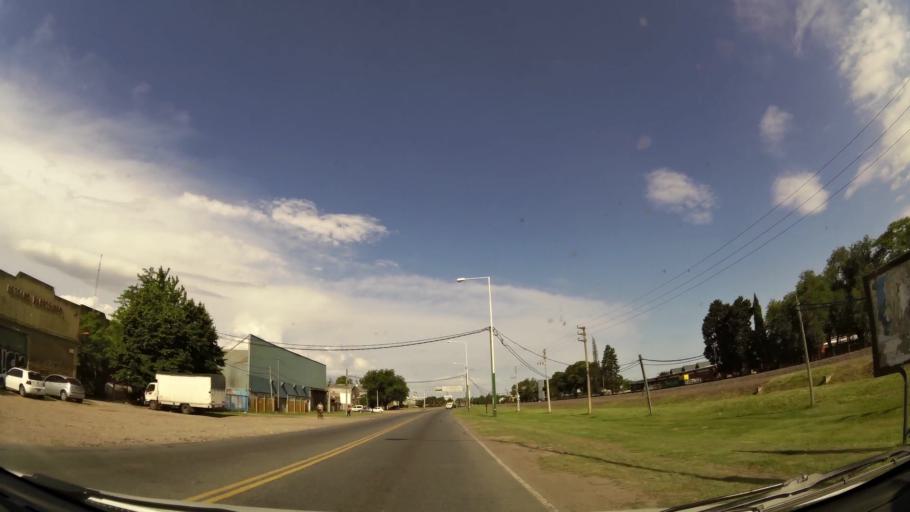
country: AR
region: Buenos Aires
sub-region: Partido de Merlo
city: Merlo
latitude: -34.6620
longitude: -58.7432
